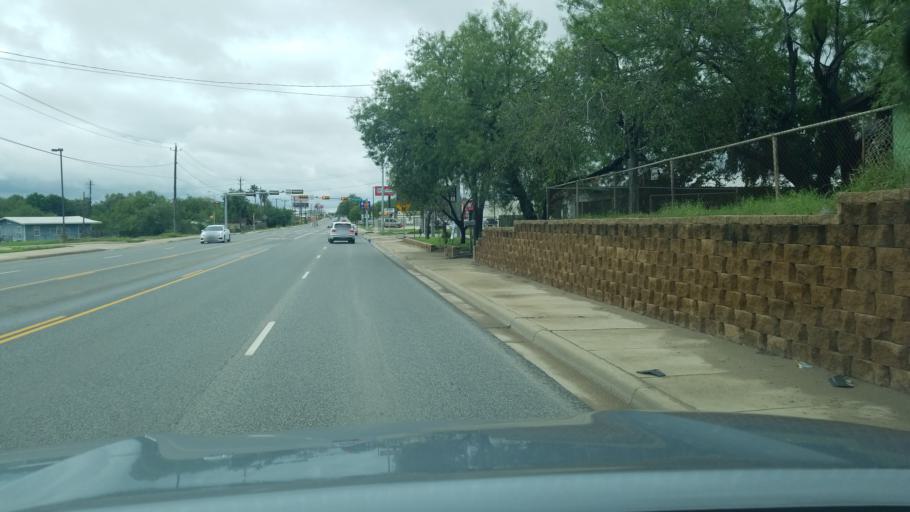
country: US
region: Texas
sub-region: Dimmit County
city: Carrizo Springs
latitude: 28.5291
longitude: -99.8539
